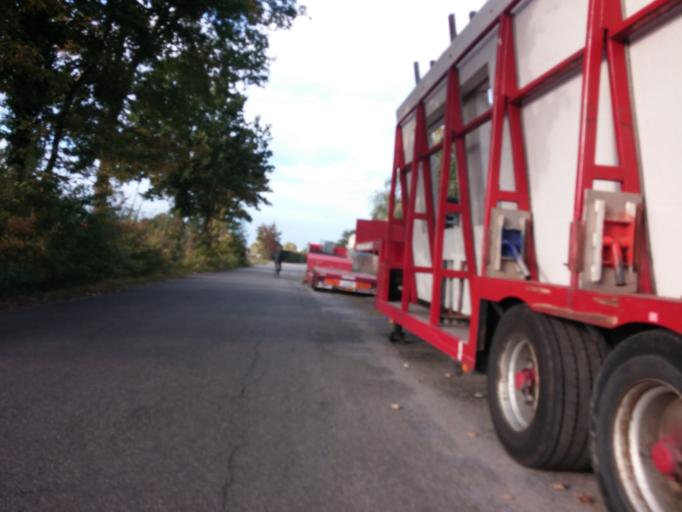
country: DE
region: North Rhine-Westphalia
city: Dorsten
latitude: 51.6533
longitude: 6.9714
